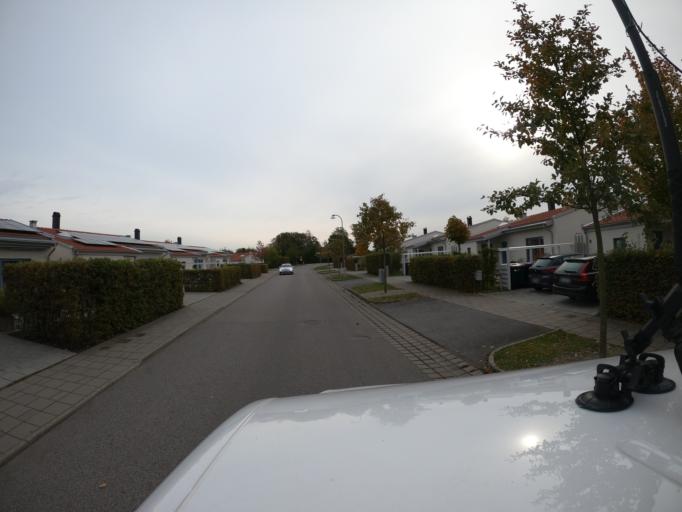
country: SE
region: Skane
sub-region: Lunds Kommun
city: Lund
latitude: 55.7485
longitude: 13.1881
